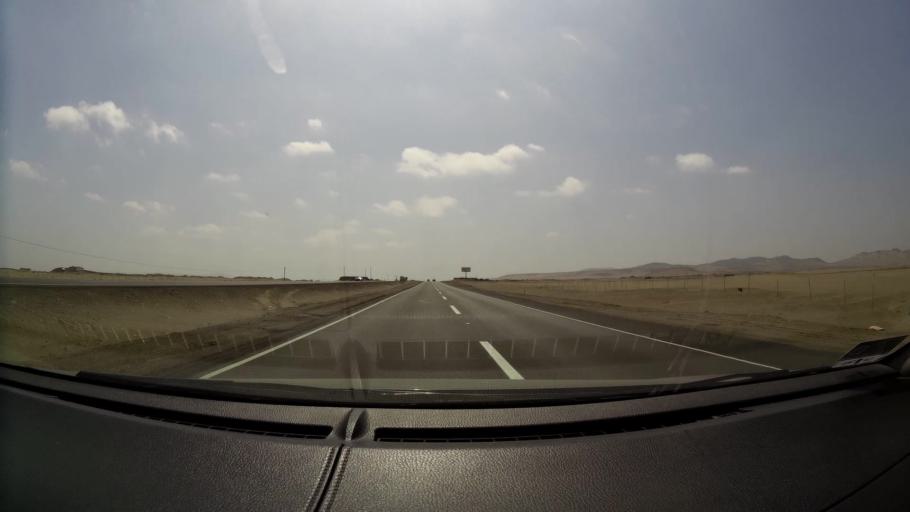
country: PE
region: Lima
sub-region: Huaura
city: Huacho
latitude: -11.3004
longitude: -77.4926
